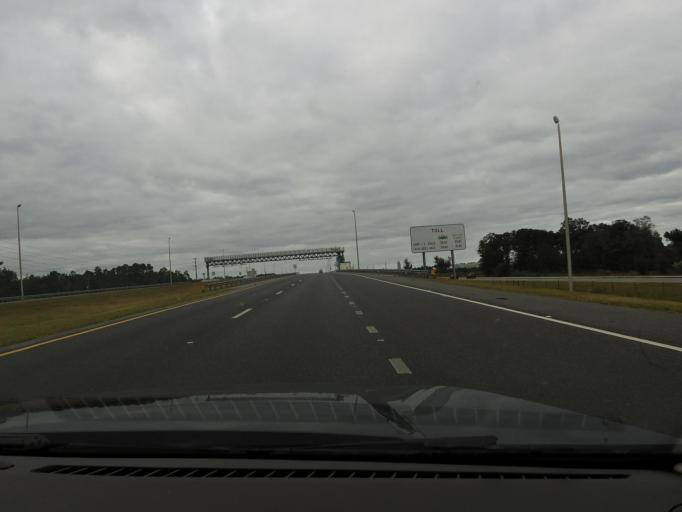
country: US
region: Florida
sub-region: Clay County
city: Lakeside
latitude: 30.1285
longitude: -81.8304
